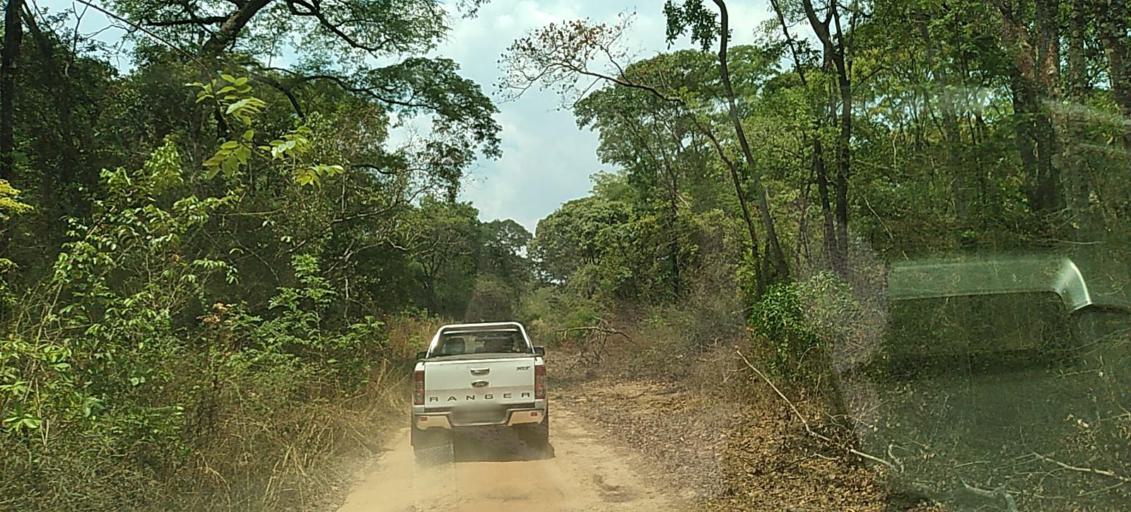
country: ZM
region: Copperbelt
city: Chingola
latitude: -12.7906
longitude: 27.6476
